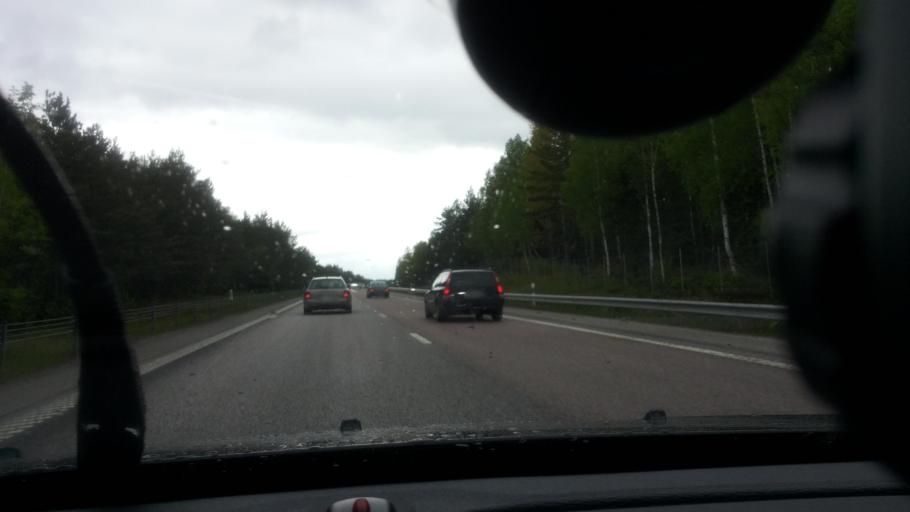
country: SE
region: Uppsala
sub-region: Knivsta Kommun
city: Knivsta
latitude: 59.7503
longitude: 17.8125
